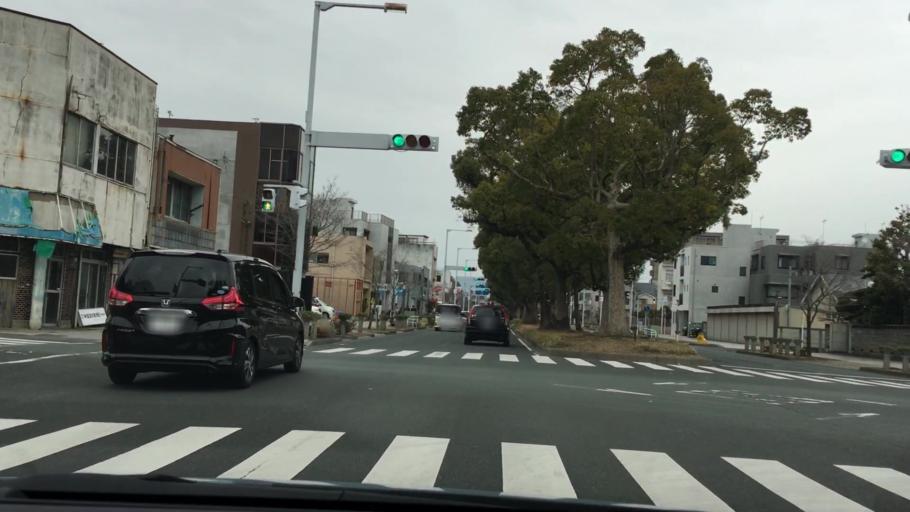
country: JP
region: Aichi
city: Toyohashi
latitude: 34.7642
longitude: 137.3947
